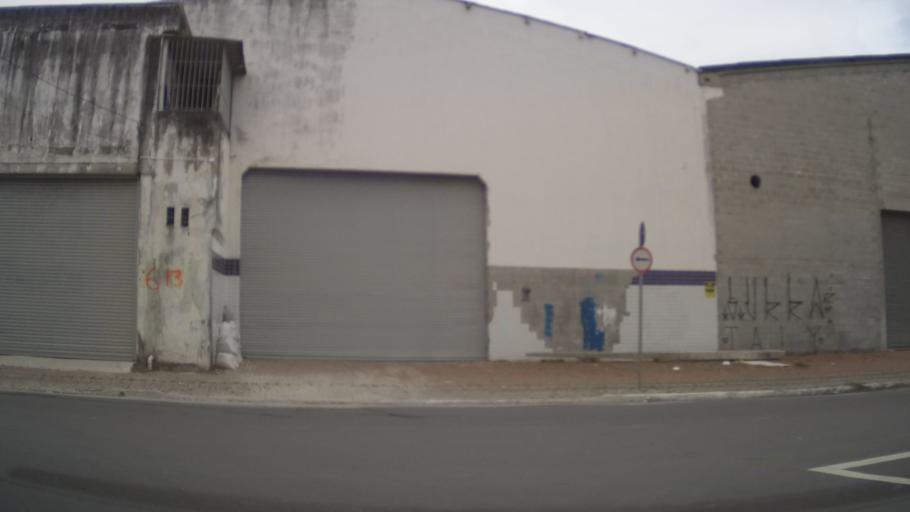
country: BR
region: Sao Paulo
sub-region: Praia Grande
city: Praia Grande
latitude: -24.0138
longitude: -46.4587
